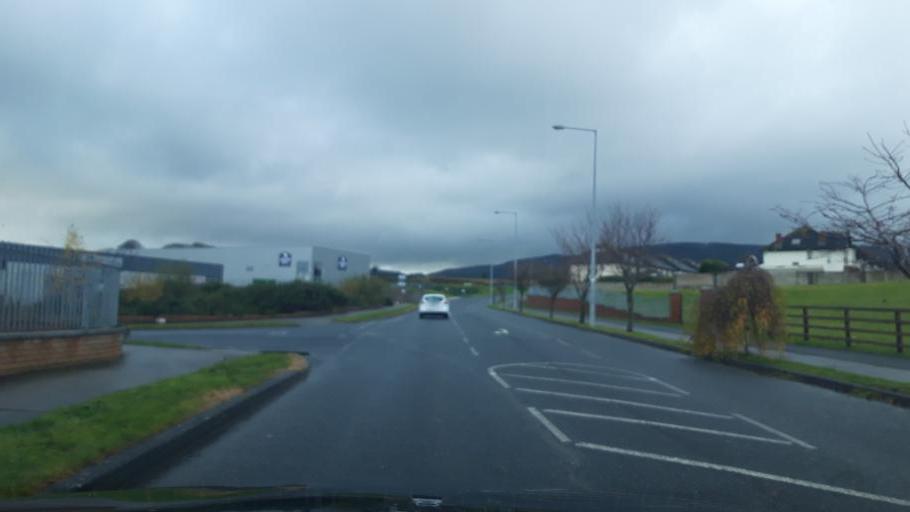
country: IE
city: Newtownmountkennedy
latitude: 53.0857
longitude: -6.1068
